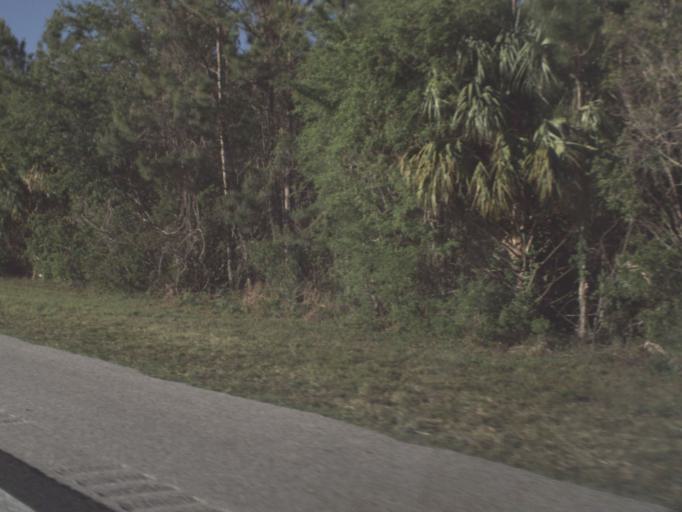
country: US
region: Florida
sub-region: Flagler County
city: Palm Coast
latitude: 29.6301
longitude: -81.2645
